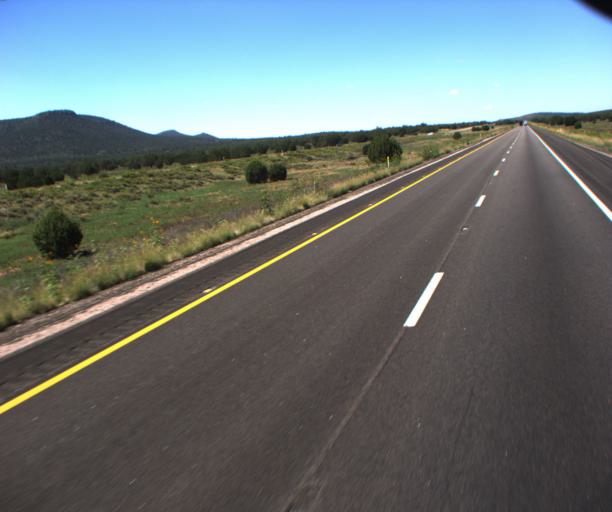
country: US
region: Arizona
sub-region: Mohave County
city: Peach Springs
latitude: 35.2201
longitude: -113.2478
